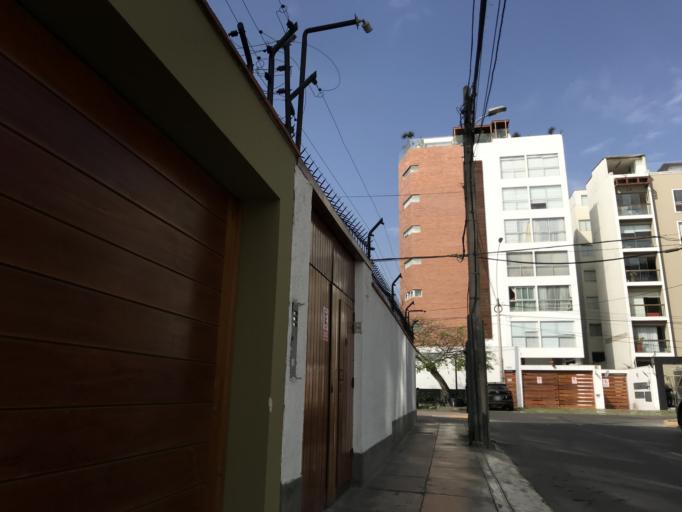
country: PE
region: Lima
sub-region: Lima
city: San Isidro
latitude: -12.1158
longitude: -77.0424
